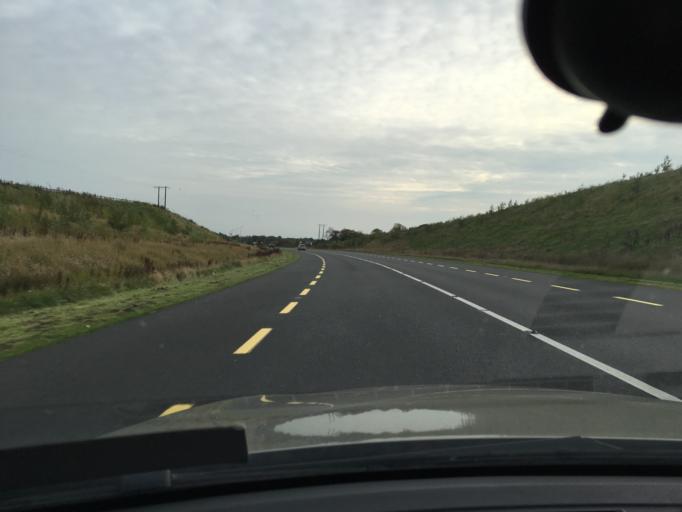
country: IE
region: Leinster
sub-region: An Longfort
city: Longford
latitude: 53.7292
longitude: -7.8252
